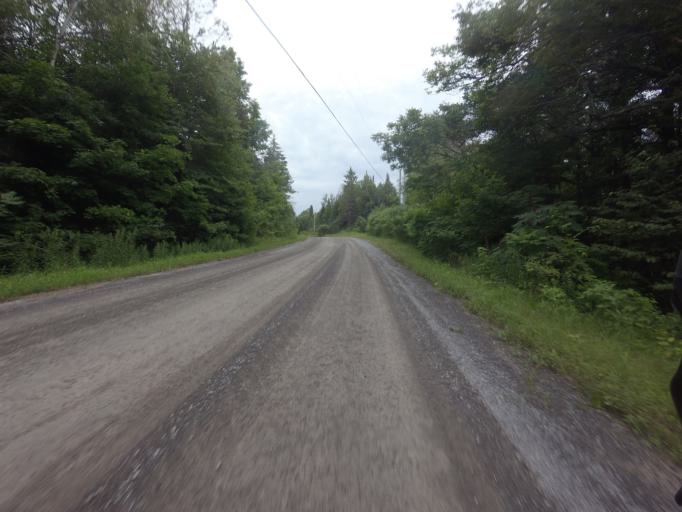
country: CA
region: Ontario
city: Carleton Place
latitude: 45.1622
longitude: -76.2710
